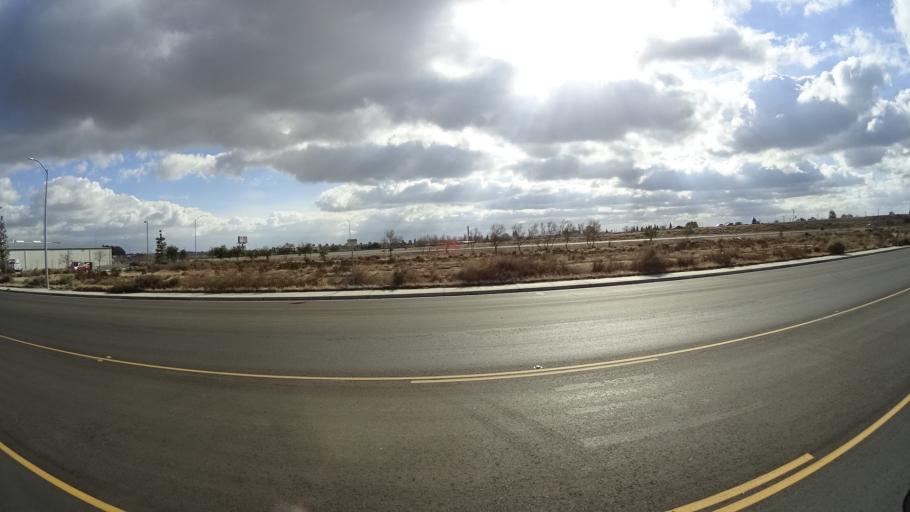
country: US
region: California
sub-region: Kern County
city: Bakersfield
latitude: 35.3541
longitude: -118.9634
